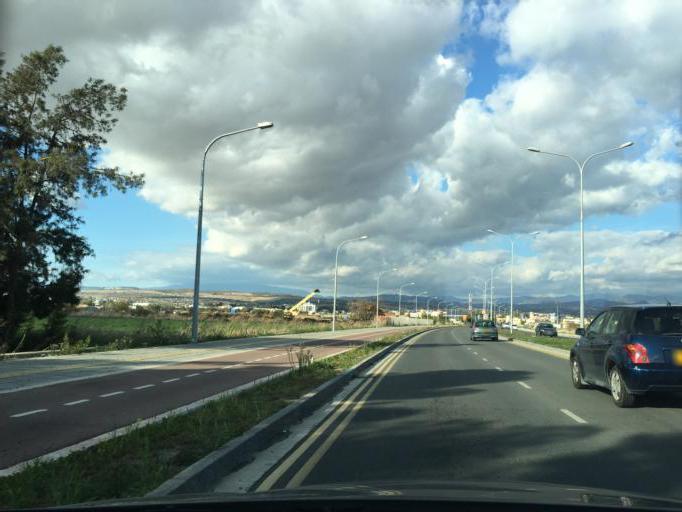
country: CY
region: Limassol
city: Ypsonas
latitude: 34.6726
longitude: 32.9887
